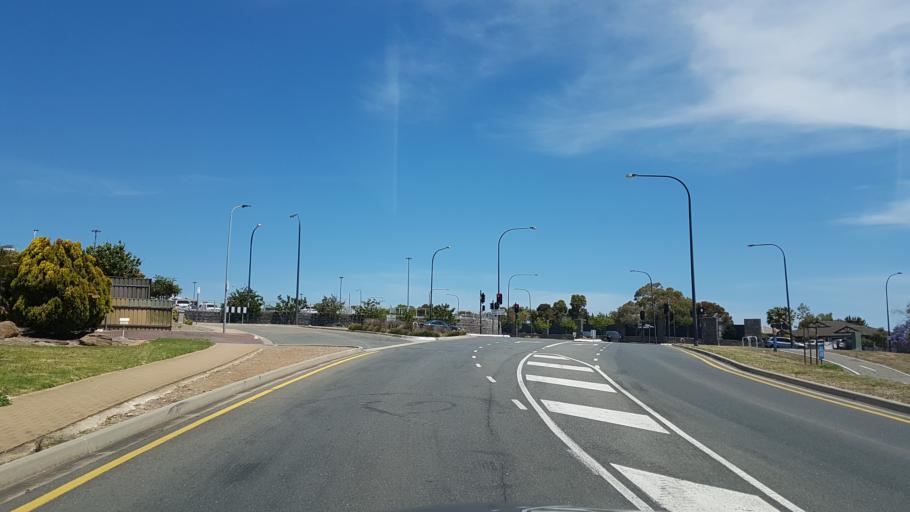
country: AU
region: South Australia
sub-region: Marion
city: Happy Valley
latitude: -35.0766
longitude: 138.5148
